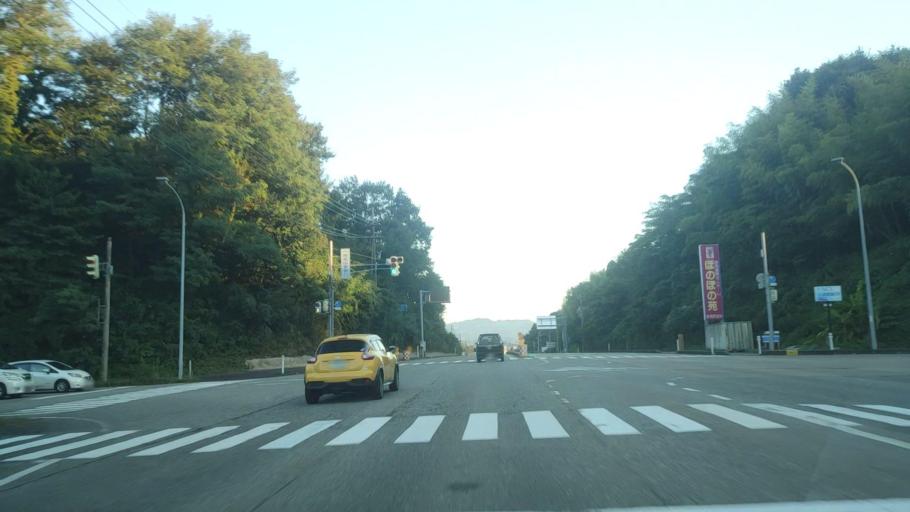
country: JP
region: Toyama
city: Himi
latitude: 36.8508
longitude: 136.9784
